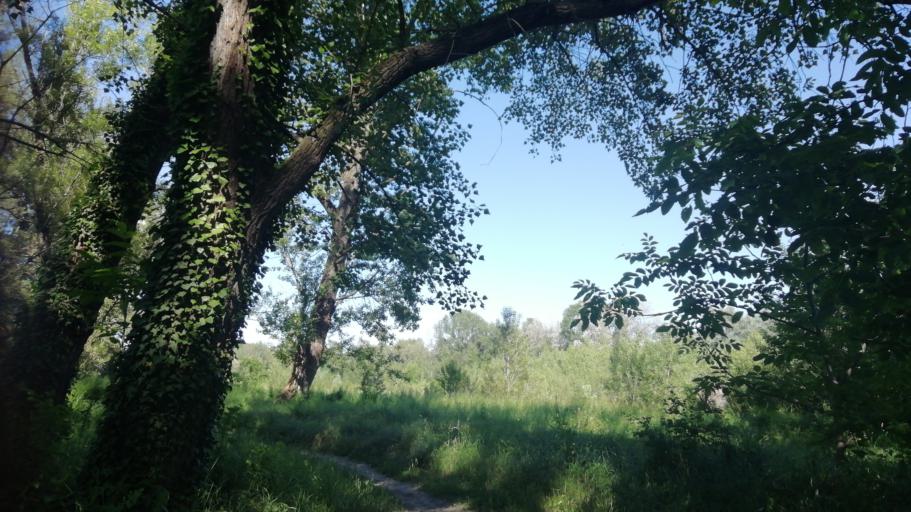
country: IT
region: Emilia-Romagna
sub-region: Provincia di Piacenza
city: Borgonovo Valtidone
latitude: 44.9793
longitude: 9.4595
